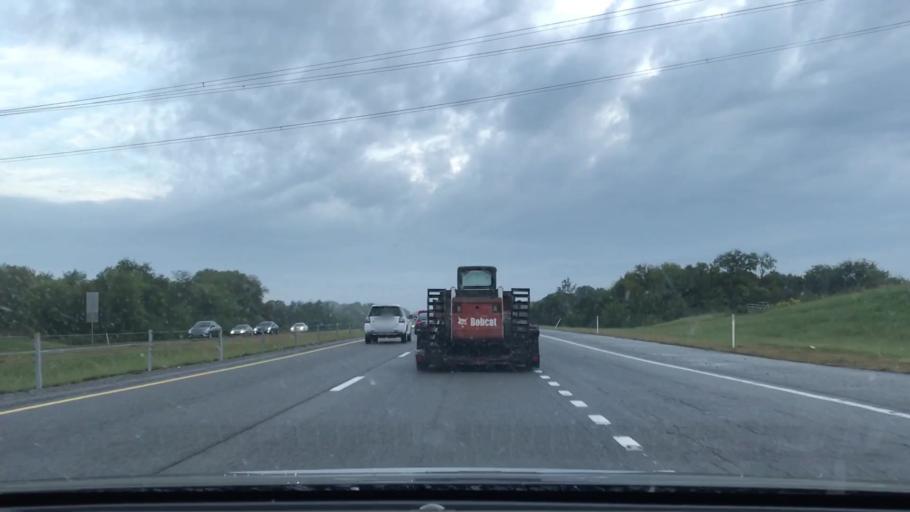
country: US
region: Tennessee
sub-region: Sumner County
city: Gallatin
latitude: 36.3620
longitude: -86.5276
